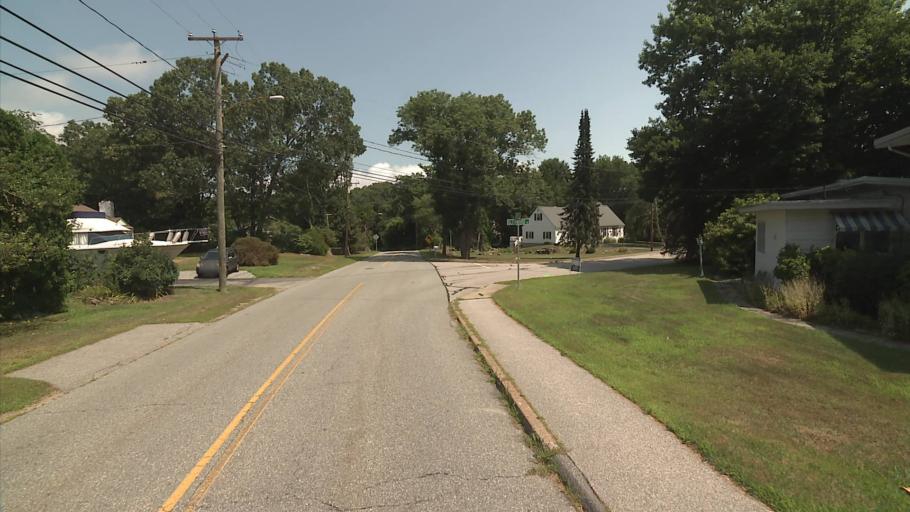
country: US
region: Connecticut
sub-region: New London County
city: Central Waterford
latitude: 41.3168
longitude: -72.1067
